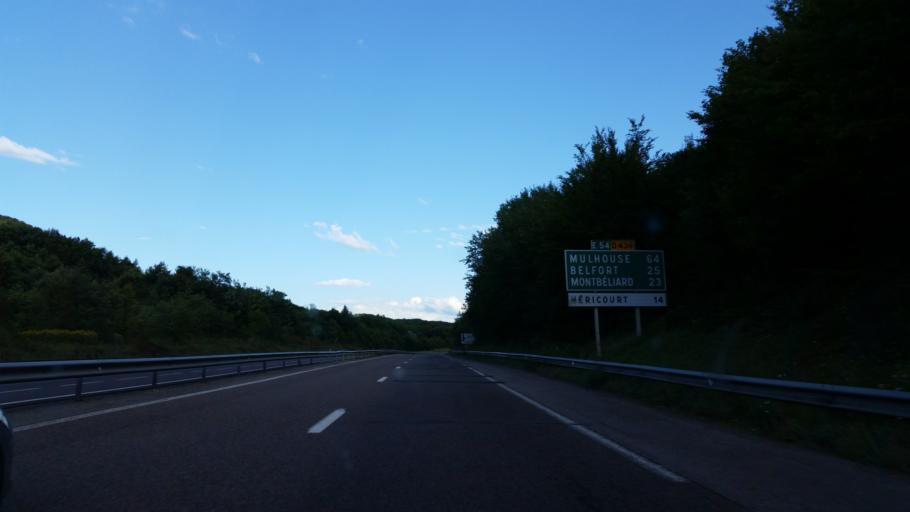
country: FR
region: Franche-Comte
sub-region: Departement de la Haute-Saone
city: Ronchamp
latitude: 47.6344
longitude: 6.6274
